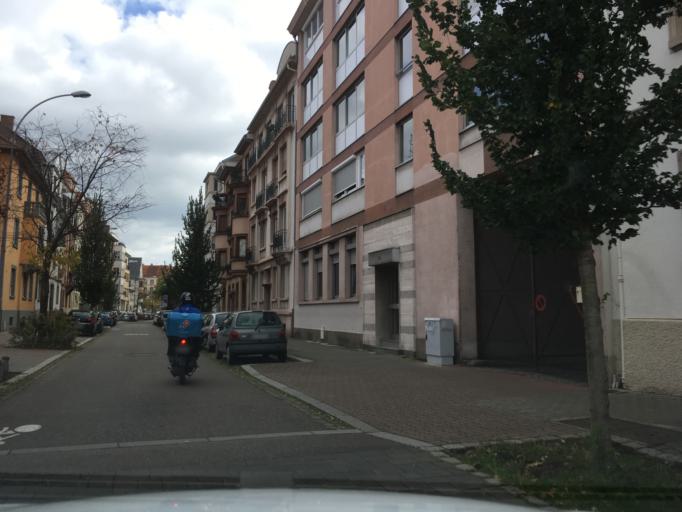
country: FR
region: Alsace
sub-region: Departement du Bas-Rhin
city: Strasbourg
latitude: 48.5659
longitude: 7.7600
